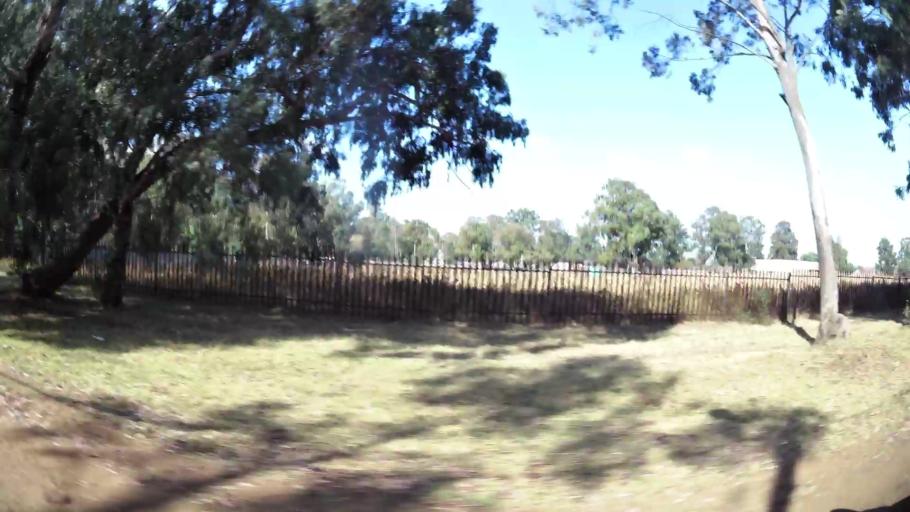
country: ZA
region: Gauteng
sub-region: Ekurhuleni Metropolitan Municipality
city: Benoni
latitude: -26.1028
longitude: 28.4052
